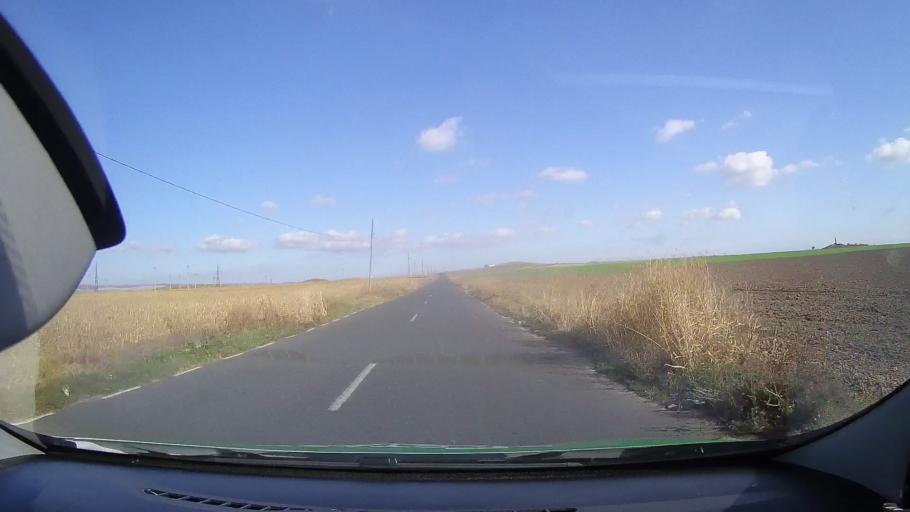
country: RO
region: Tulcea
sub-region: Comuna Ceamurlia de Jos
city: Ceamurlia de Jos
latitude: 44.7383
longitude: 28.6909
